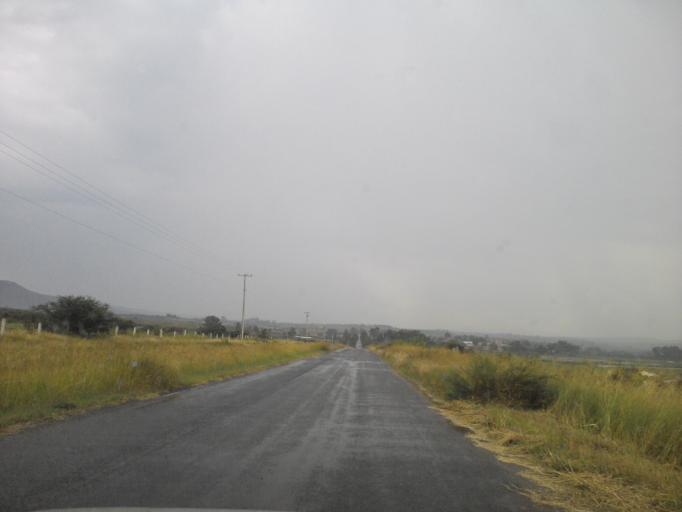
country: MX
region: Jalisco
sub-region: Arandas
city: Santiaguito (Santiaguito de Velazquez)
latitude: 20.8348
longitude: -102.1076
